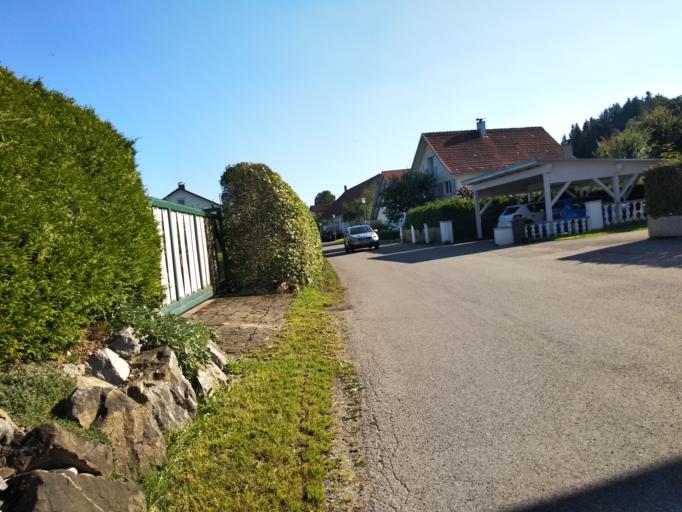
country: DE
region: Baden-Wuerttemberg
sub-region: Tuebingen Region
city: Leutkirch im Allgau
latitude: 47.7772
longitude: 10.0414
